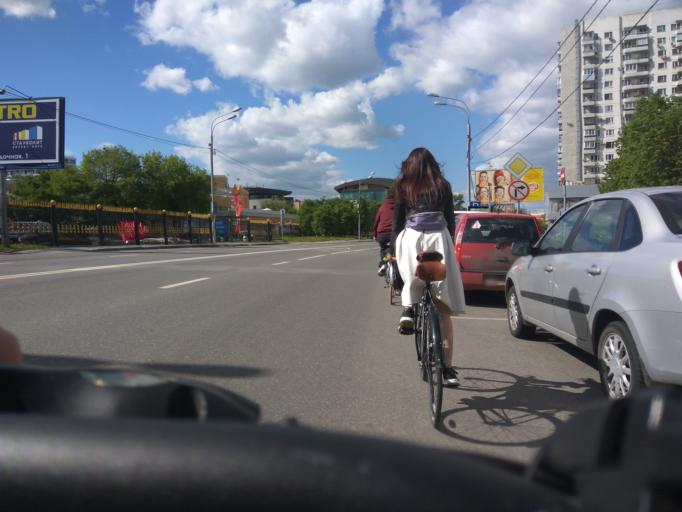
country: RU
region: Moscow
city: Mar'ina Roshcha
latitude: 55.7850
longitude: 37.6229
